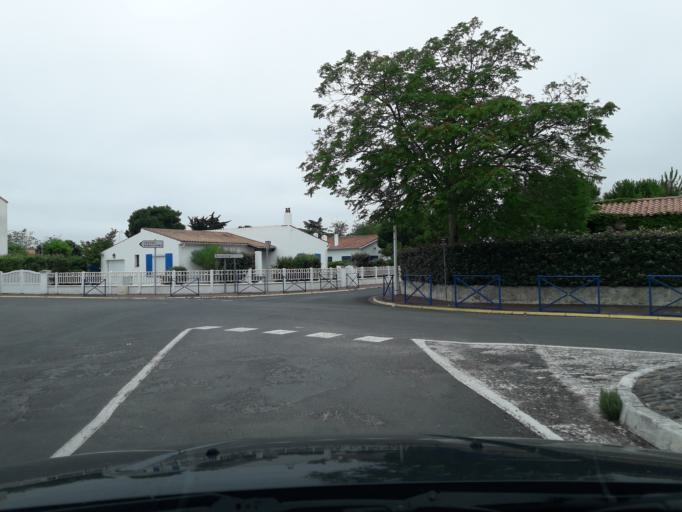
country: FR
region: Poitou-Charentes
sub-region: Departement de la Charente-Maritime
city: Boyard-Ville
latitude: 45.9676
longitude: -1.2438
